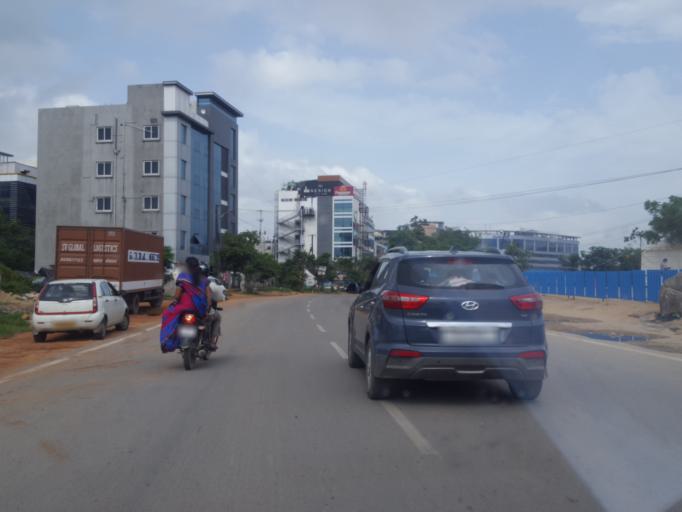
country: IN
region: Telangana
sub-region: Rangareddi
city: Kukatpalli
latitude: 17.4412
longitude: 78.3749
